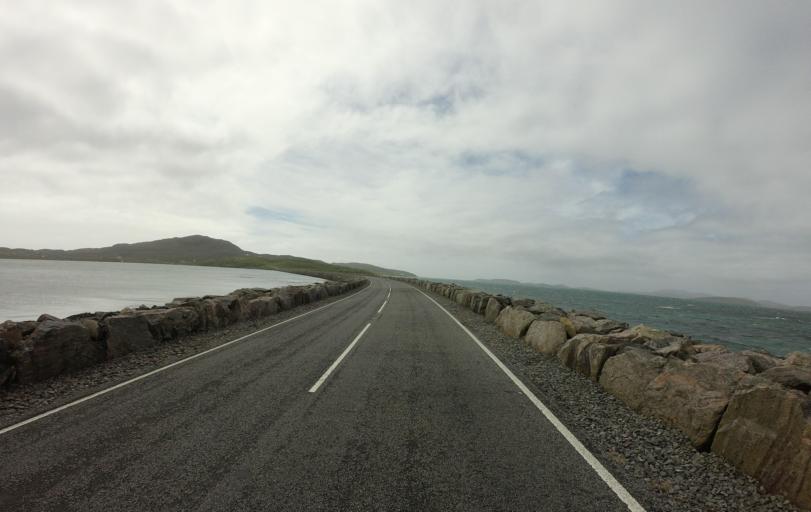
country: GB
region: Scotland
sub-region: Eilean Siar
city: Isle of South Uist
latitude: 57.0948
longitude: -7.3177
